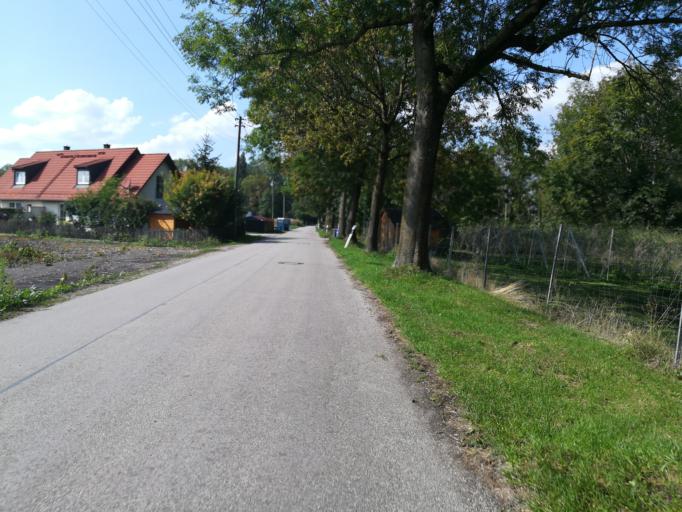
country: DE
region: Bavaria
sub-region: Upper Bavaria
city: Karlsfeld
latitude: 48.2258
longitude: 11.5138
